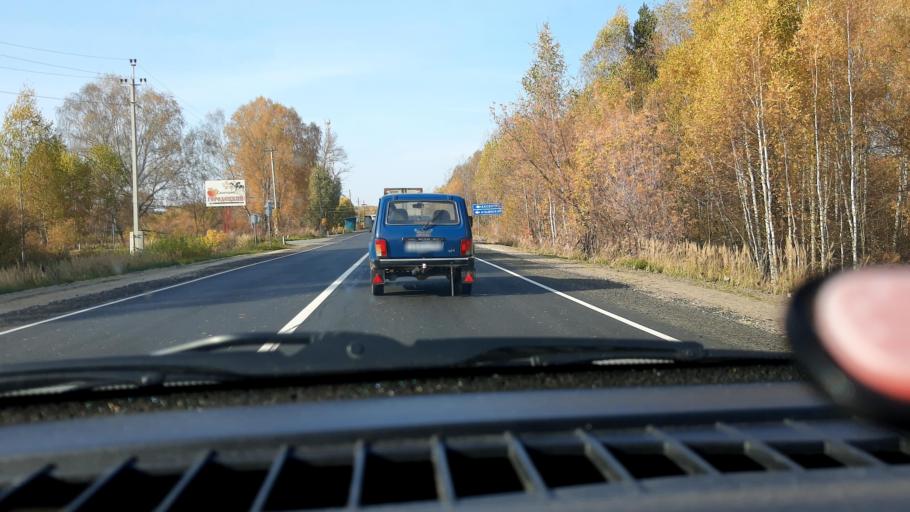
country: RU
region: Nizjnij Novgorod
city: Novaya Balakhna
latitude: 56.5974
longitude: 43.6422
